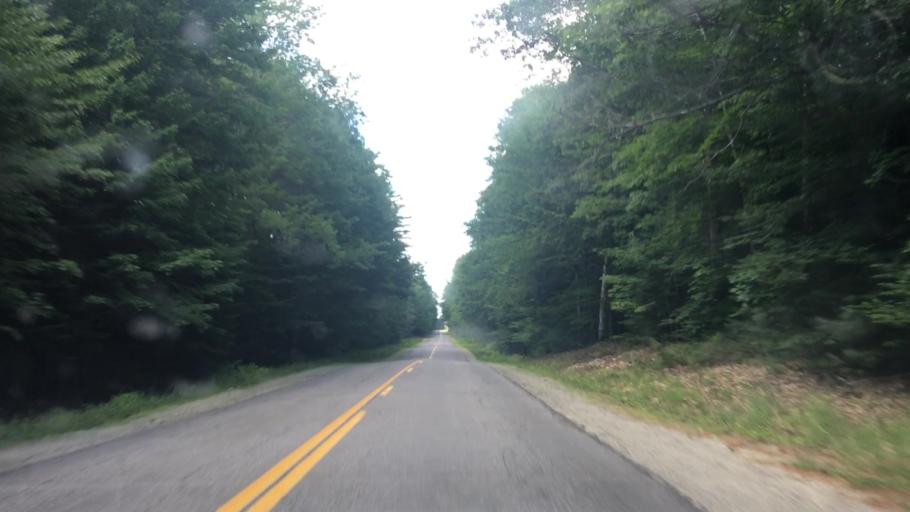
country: US
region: Maine
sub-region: Franklin County
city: Chesterville
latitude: 44.5961
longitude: -70.0853
